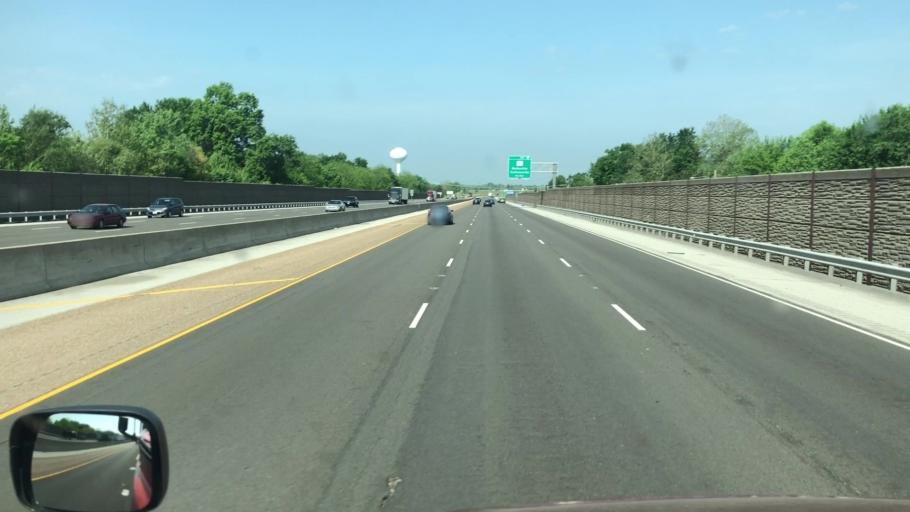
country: US
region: Illinois
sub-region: Saint Clair County
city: Fairview Heights
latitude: 38.5993
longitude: -89.9687
